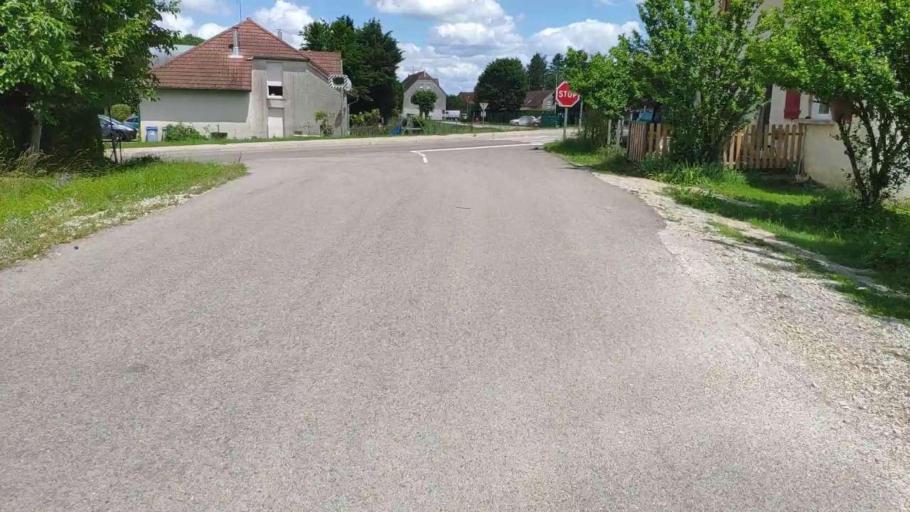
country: FR
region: Franche-Comte
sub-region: Departement du Jura
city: Bletterans
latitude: 46.8457
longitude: 5.4821
